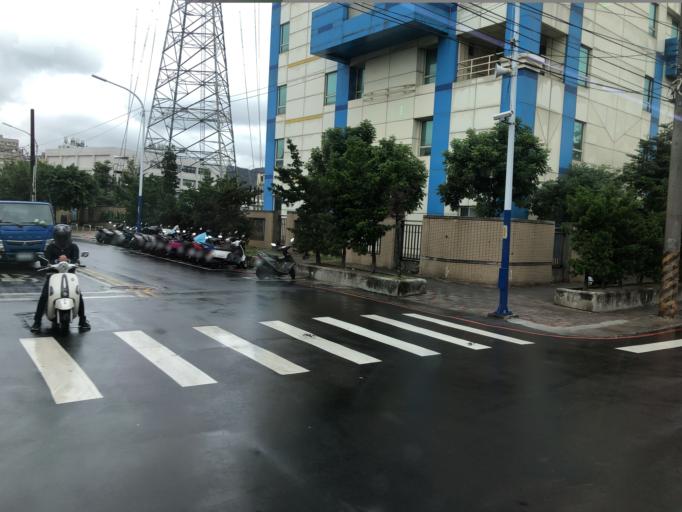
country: TW
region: Taipei
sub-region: Taipei
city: Banqiao
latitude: 25.0287
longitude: 121.4263
